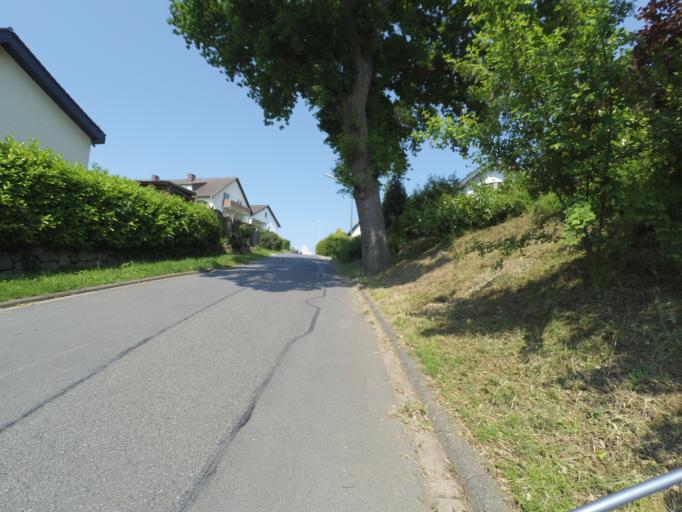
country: DE
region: Rheinland-Pfalz
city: Kehrig
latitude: 50.3028
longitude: 7.2242
